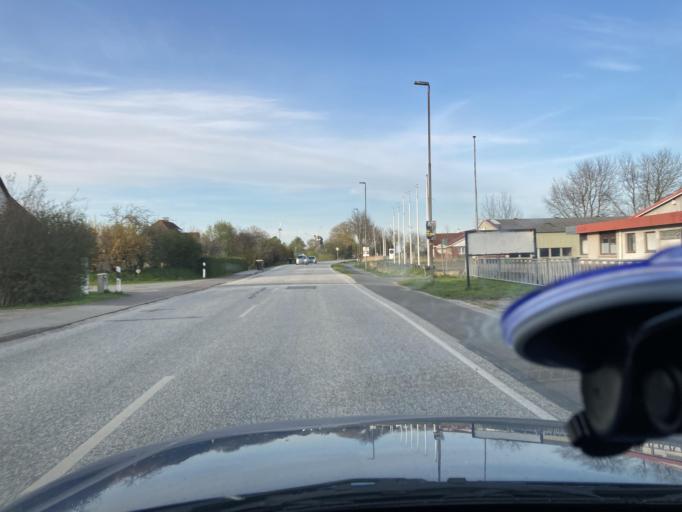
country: DE
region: Schleswig-Holstein
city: Wohrden
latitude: 54.1671
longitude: 8.9998
